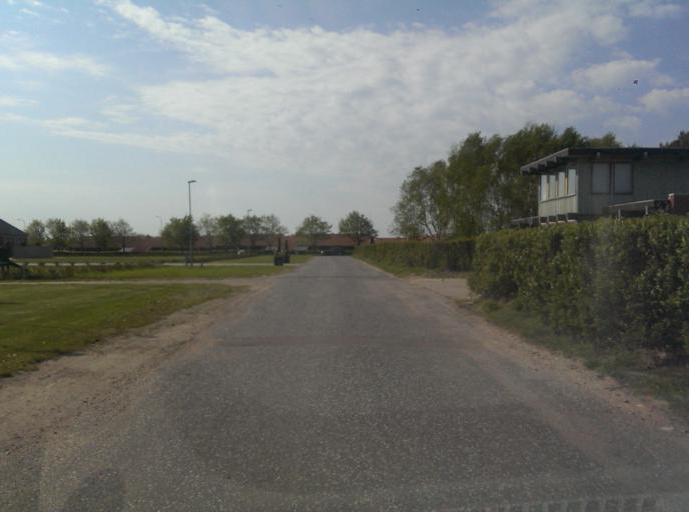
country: DK
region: South Denmark
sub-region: Esbjerg Kommune
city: Tjaereborg
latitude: 55.4609
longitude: 8.5947
